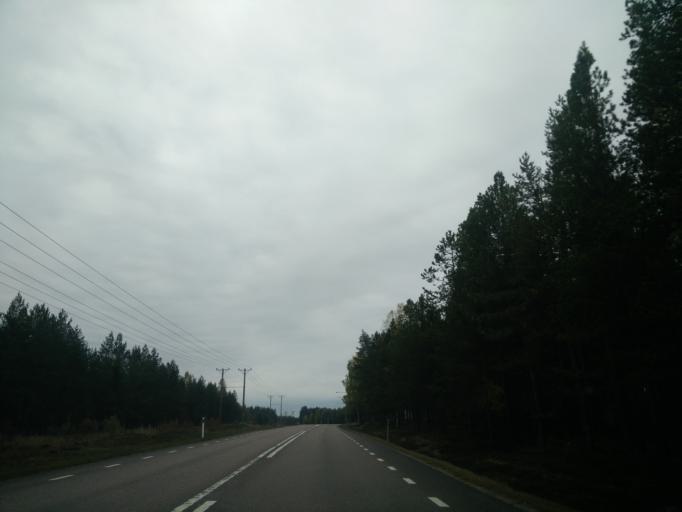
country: SE
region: Gaevleborg
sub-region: Gavle Kommun
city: Gavle
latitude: 60.8081
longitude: 17.2122
